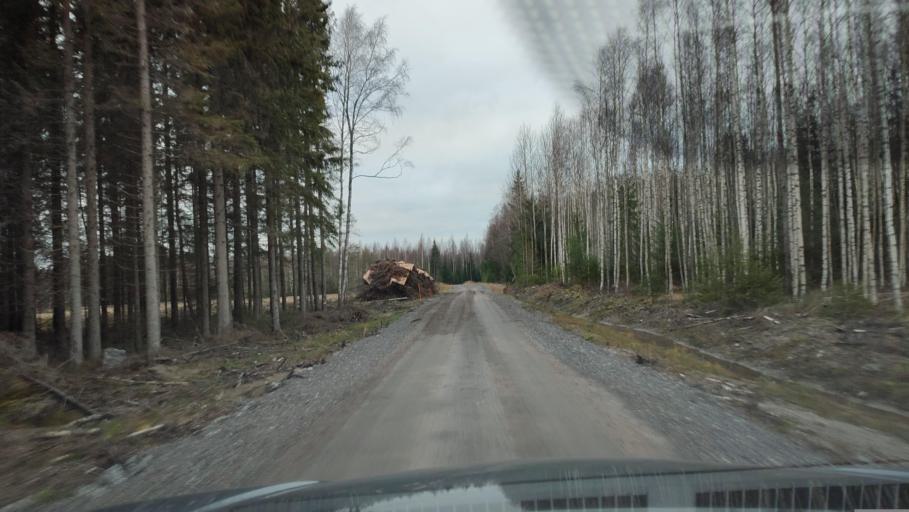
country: FI
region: Southern Ostrobothnia
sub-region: Suupohja
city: Karijoki
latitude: 62.2174
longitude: 21.6012
